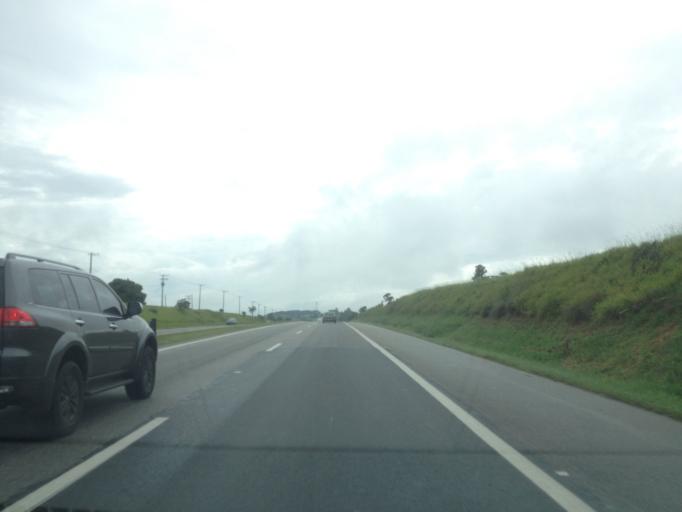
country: BR
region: Sao Paulo
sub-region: Itu
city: Itu
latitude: -23.3512
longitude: -47.3252
